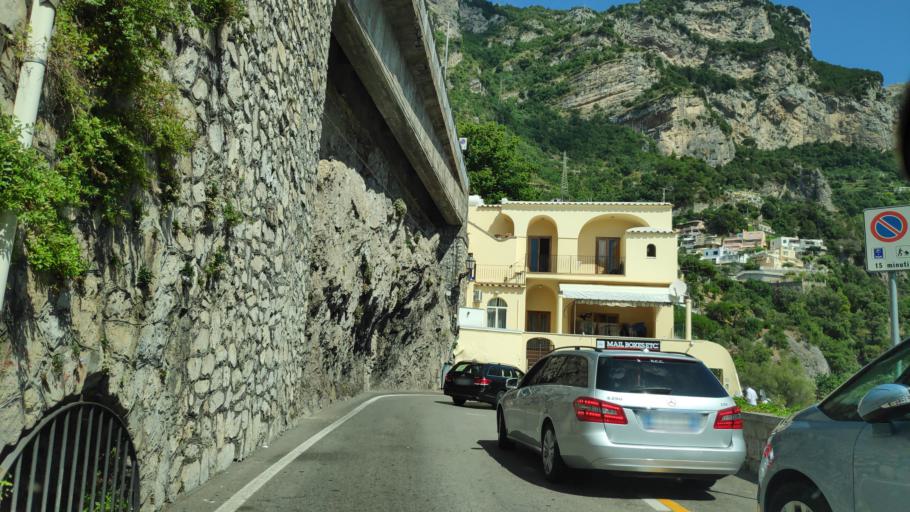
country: IT
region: Campania
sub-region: Provincia di Salerno
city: Positano
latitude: 40.6297
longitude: 14.4823
